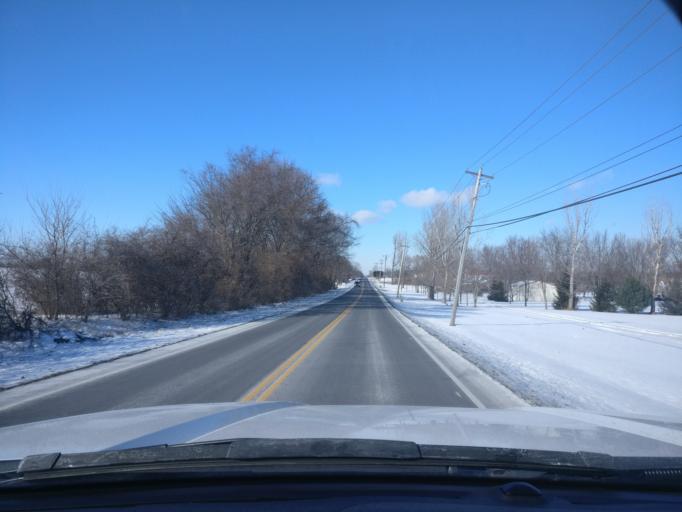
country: US
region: Ohio
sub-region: Warren County
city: Hunter
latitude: 39.5150
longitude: -84.2707
